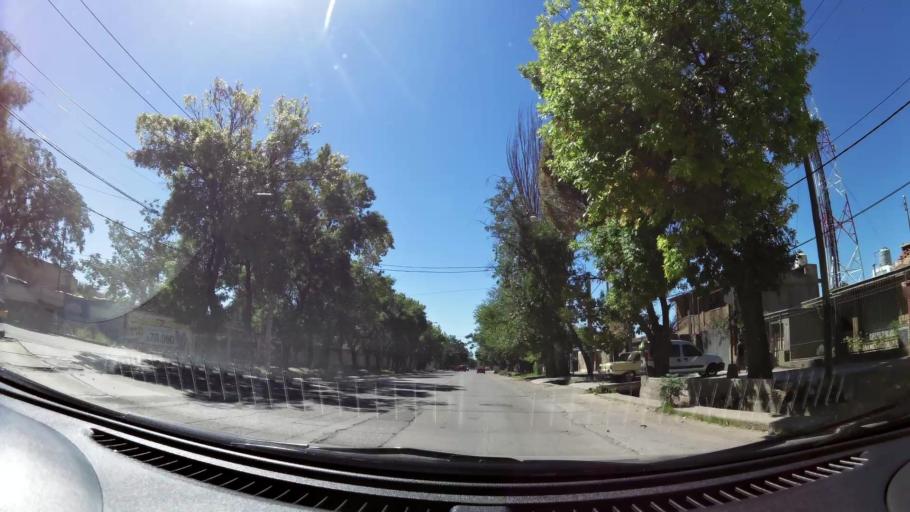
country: AR
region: Mendoza
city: Las Heras
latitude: -32.8402
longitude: -68.8337
